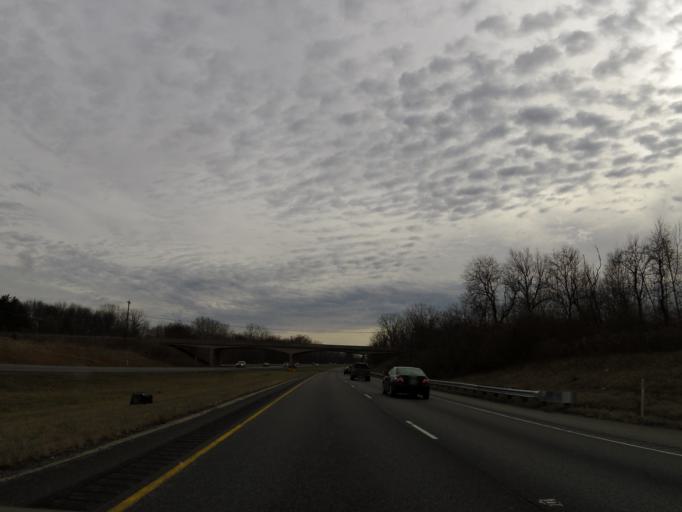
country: US
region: Indiana
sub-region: Hendricks County
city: Pittsboro
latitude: 39.8794
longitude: -86.4415
